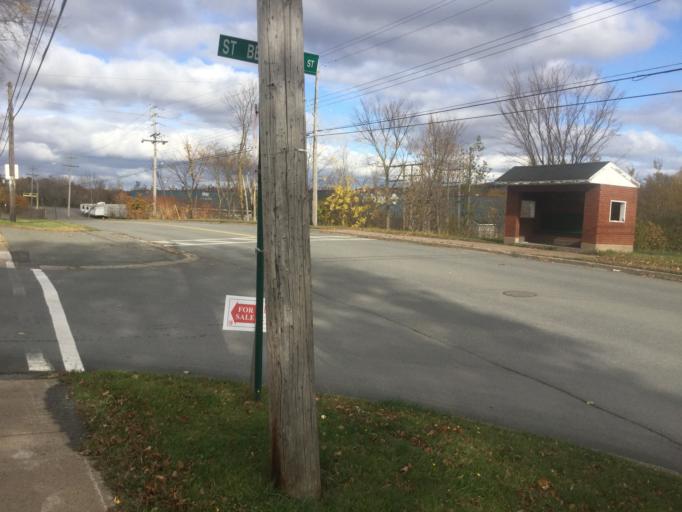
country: CA
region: Nova Scotia
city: New Glasgow
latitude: 45.5754
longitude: -62.6563
